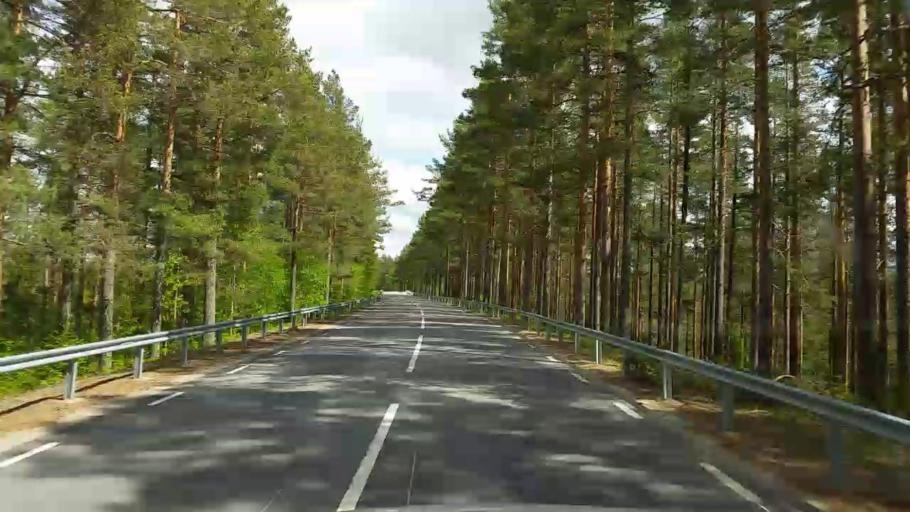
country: SE
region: Gaevleborg
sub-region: Bollnas Kommun
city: Vittsjo
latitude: 61.1218
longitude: 16.1665
